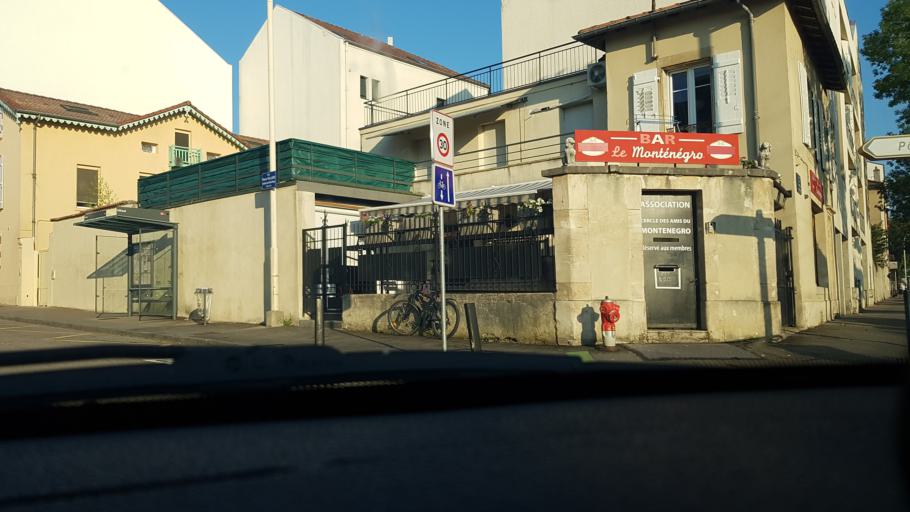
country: FR
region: Lorraine
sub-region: Departement de Meurthe-et-Moselle
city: Nancy
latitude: 48.6802
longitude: 6.1882
